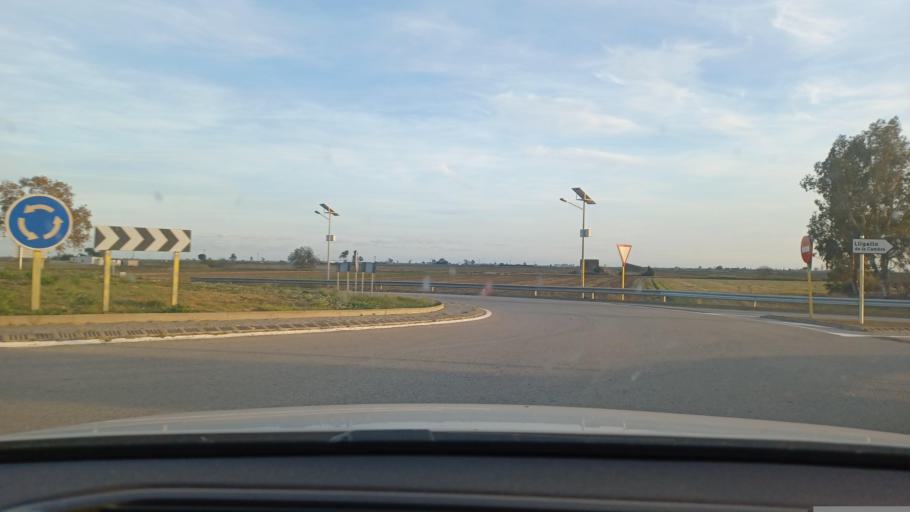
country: ES
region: Catalonia
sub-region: Provincia de Tarragona
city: Amposta
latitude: 40.7045
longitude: 0.6320
